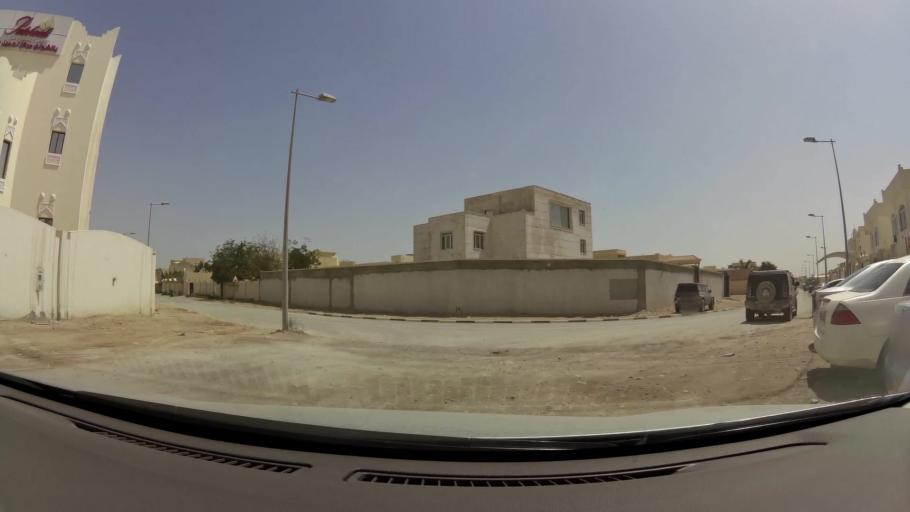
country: QA
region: Baladiyat Umm Salal
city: Umm Salal Muhammad
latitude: 25.4029
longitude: 51.4346
